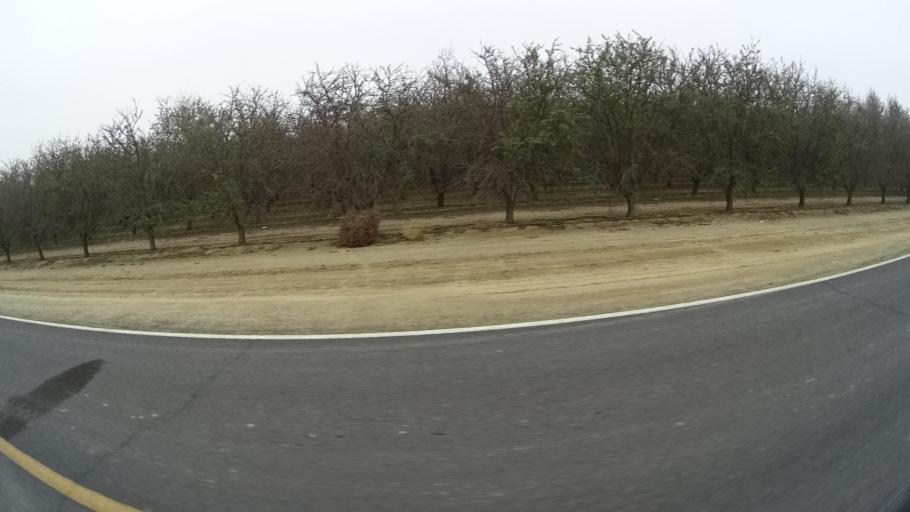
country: US
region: California
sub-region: Kern County
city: Lost Hills
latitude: 35.6103
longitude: -119.5803
